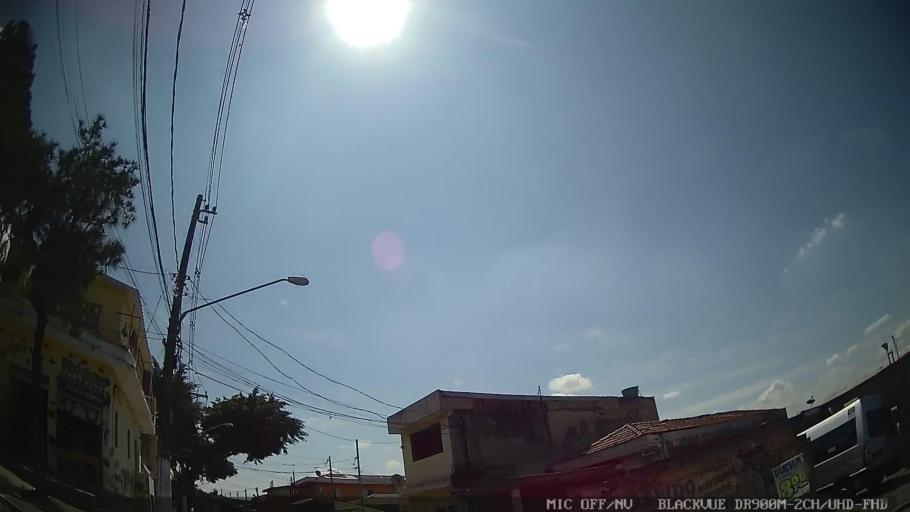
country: BR
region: Sao Paulo
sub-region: Guarulhos
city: Guarulhos
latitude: -23.5011
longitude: -46.5136
